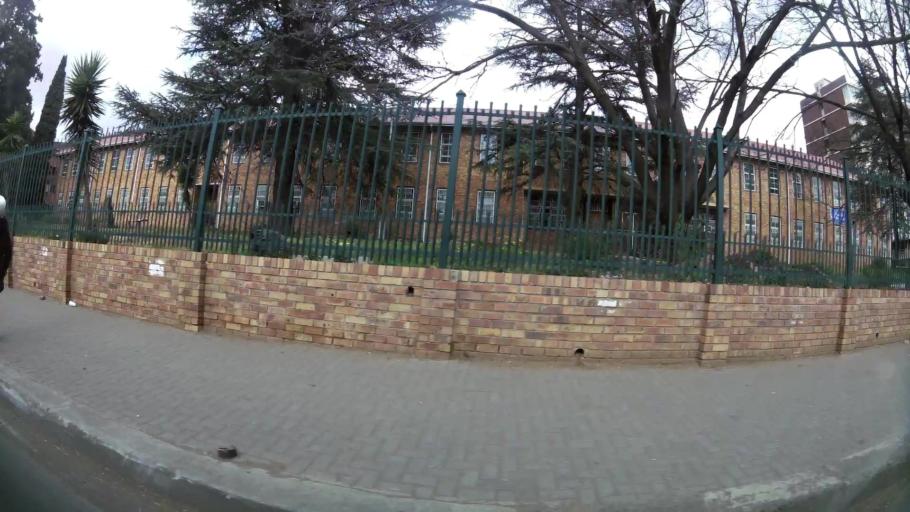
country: ZA
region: Orange Free State
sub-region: Mangaung Metropolitan Municipality
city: Bloemfontein
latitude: -29.1214
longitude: 26.2220
